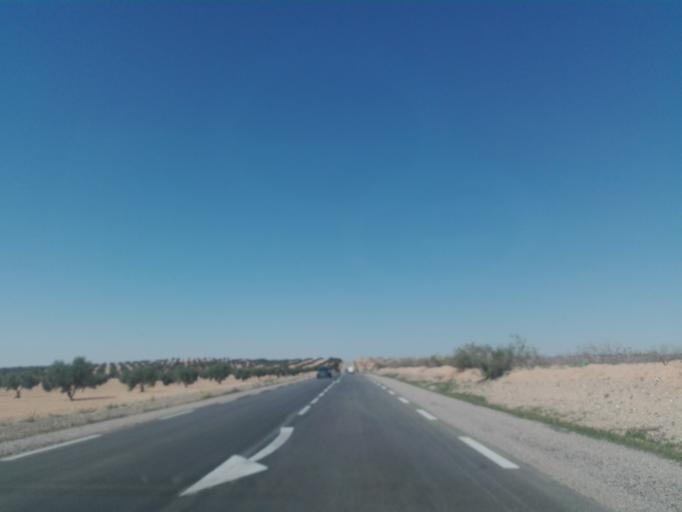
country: TN
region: Safaqis
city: Bi'r `Ali Bin Khalifah
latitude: 34.7583
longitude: 10.2881
